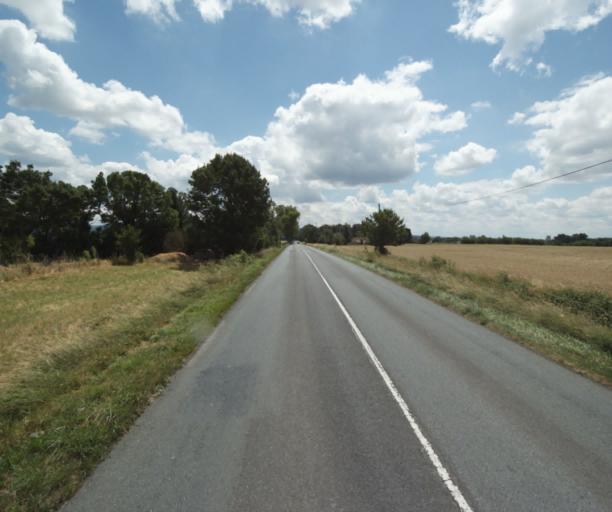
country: FR
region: Midi-Pyrenees
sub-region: Departement de la Haute-Garonne
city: Revel
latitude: 43.5025
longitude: 2.0117
